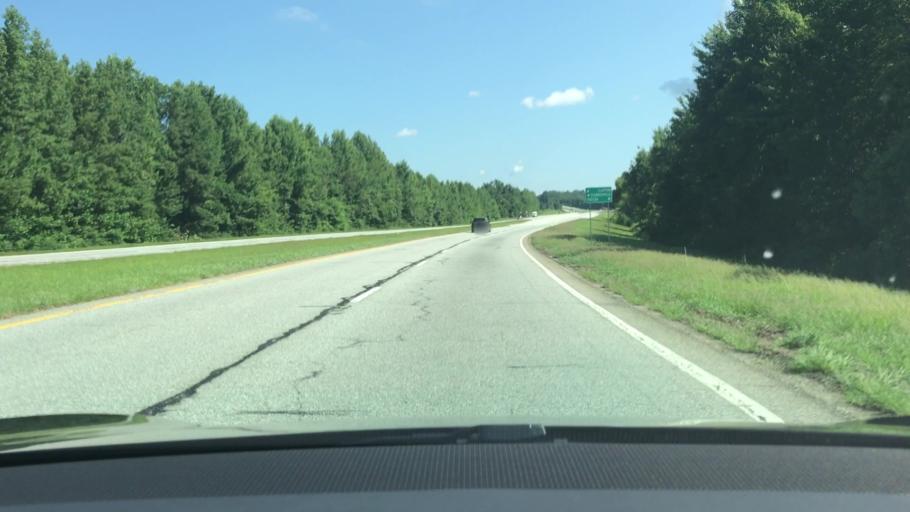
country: US
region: Georgia
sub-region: Habersham County
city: Clarkesville
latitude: 34.6104
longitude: -83.4493
